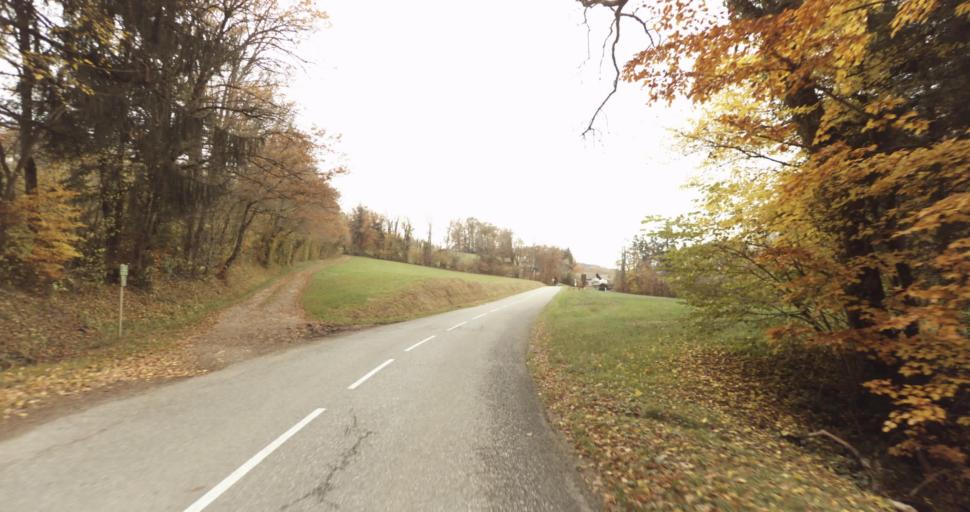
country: FR
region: Rhone-Alpes
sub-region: Departement de la Haute-Savoie
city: Saint-Martin-Bellevue
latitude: 45.9671
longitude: 6.1471
